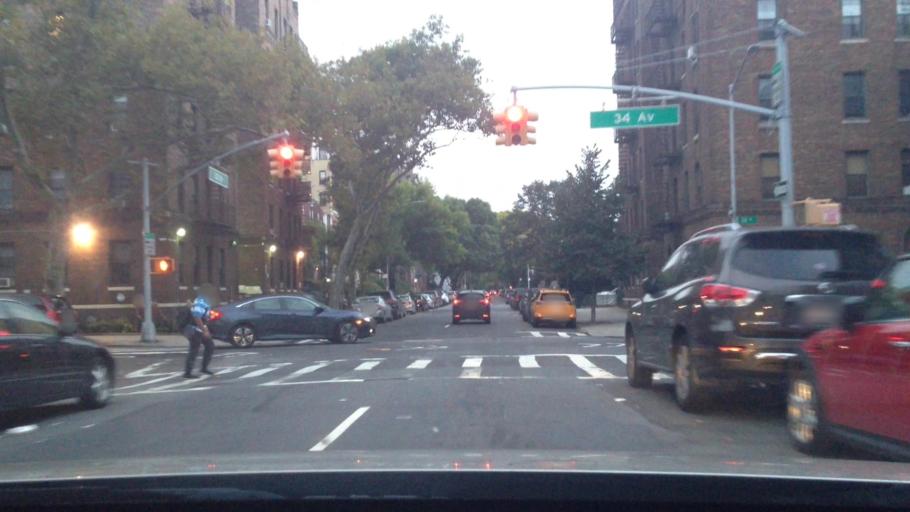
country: US
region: New York
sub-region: Queens County
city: Long Island City
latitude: 40.7588
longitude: -73.9258
